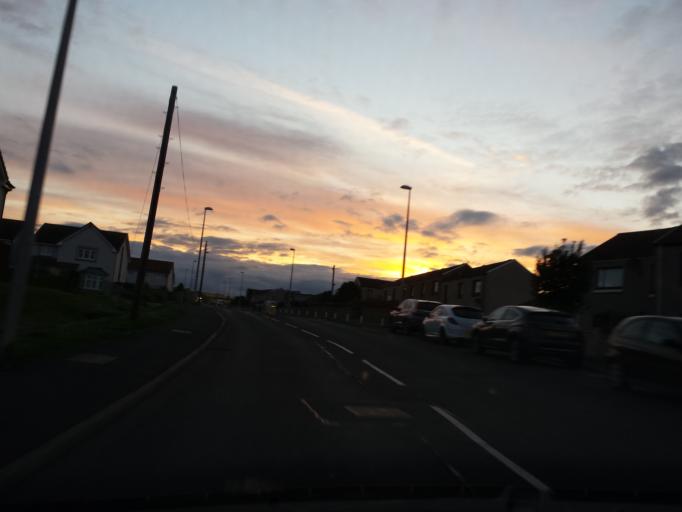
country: GB
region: Scotland
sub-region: The Scottish Borders
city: Eyemouth
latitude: 55.8716
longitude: -2.1027
